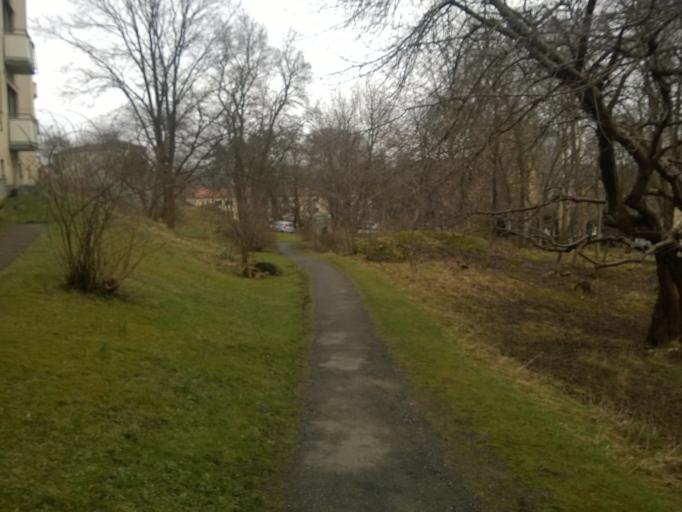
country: SE
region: Vaestra Goetaland
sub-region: Goteborg
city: Goeteborg
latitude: 57.6907
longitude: 11.9659
